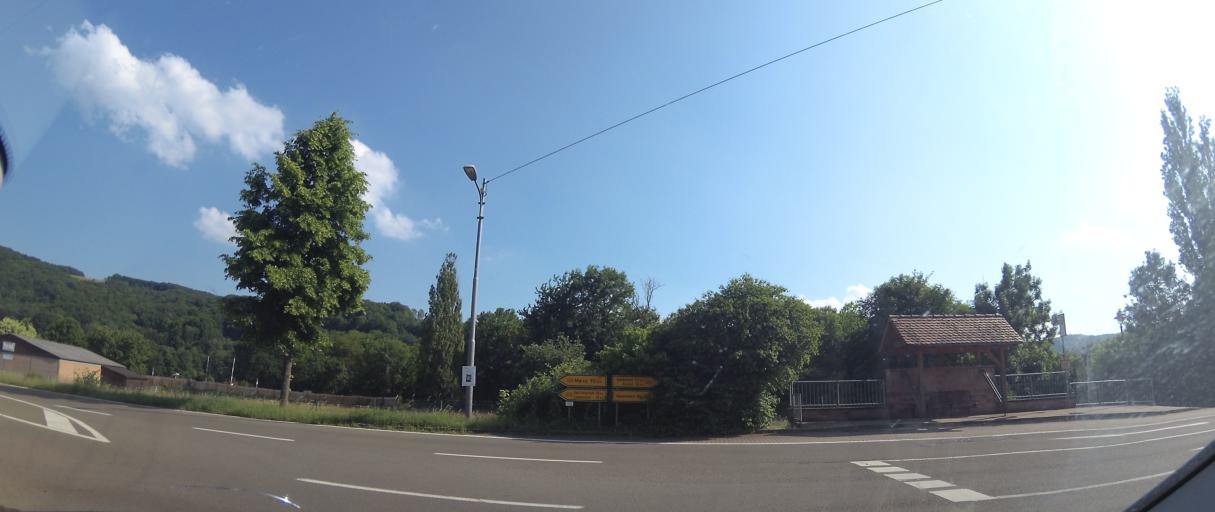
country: DE
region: Rheinland-Pfalz
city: Rathsweiler
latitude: 49.5978
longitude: 7.4650
